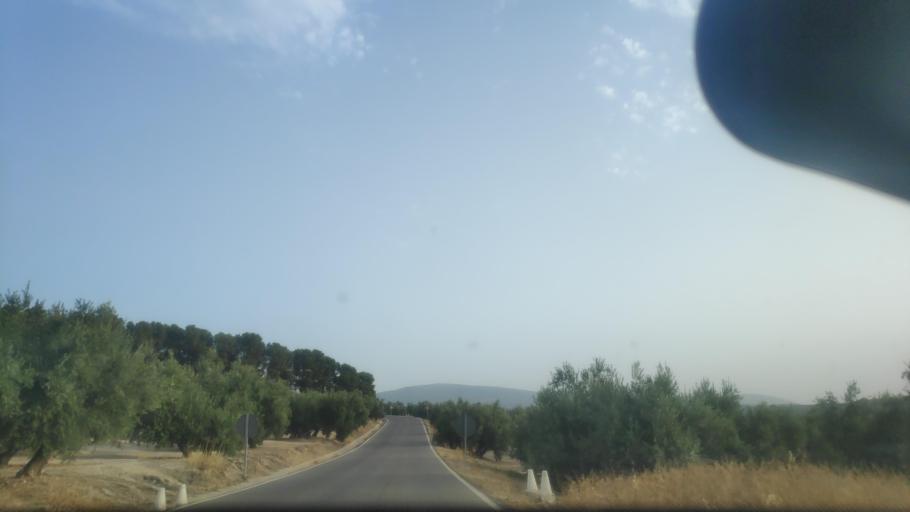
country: ES
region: Andalusia
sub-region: Provincia de Jaen
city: Jimena
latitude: 37.8390
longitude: -3.5294
